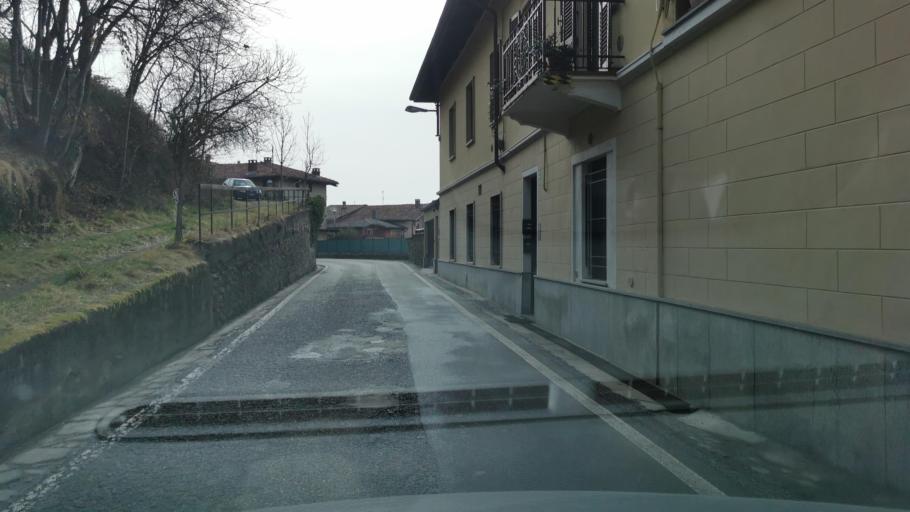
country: IT
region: Piedmont
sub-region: Provincia di Biella
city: Pollone
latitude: 45.5825
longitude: 8.0102
